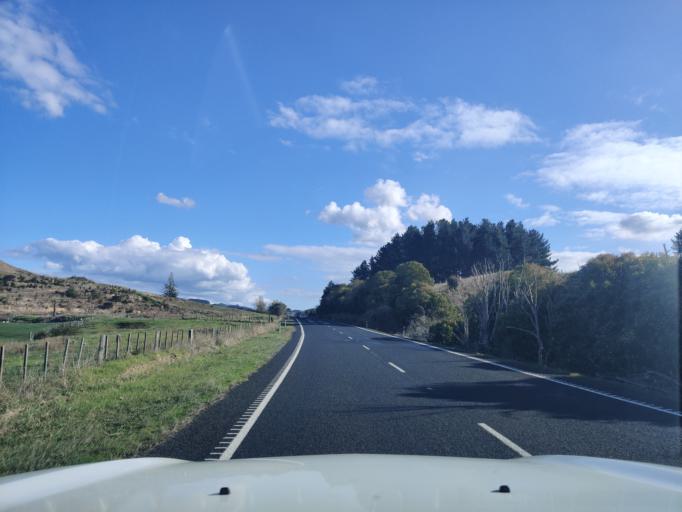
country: NZ
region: Waikato
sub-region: Hauraki District
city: Ngatea
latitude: -37.2818
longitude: 175.4029
